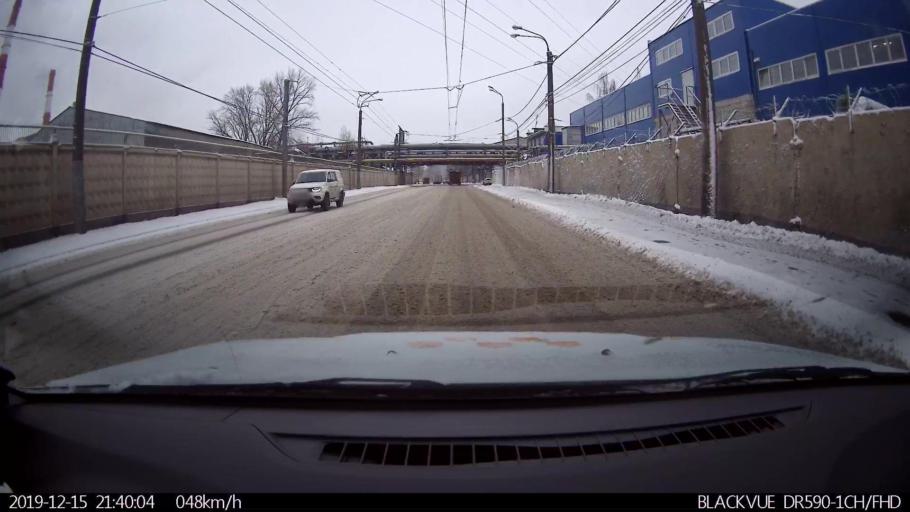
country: RU
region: Nizjnij Novgorod
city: Nizhniy Novgorod
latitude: 56.2399
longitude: 43.8937
